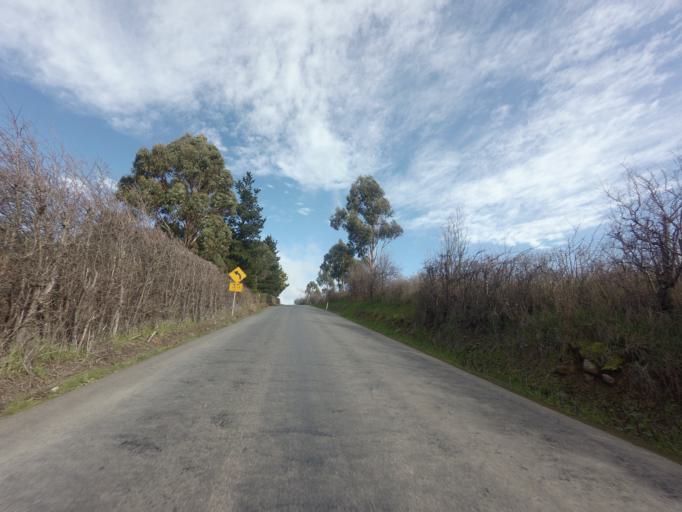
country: AU
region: Tasmania
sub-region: Derwent Valley
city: New Norfolk
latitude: -42.7749
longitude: 147.0214
